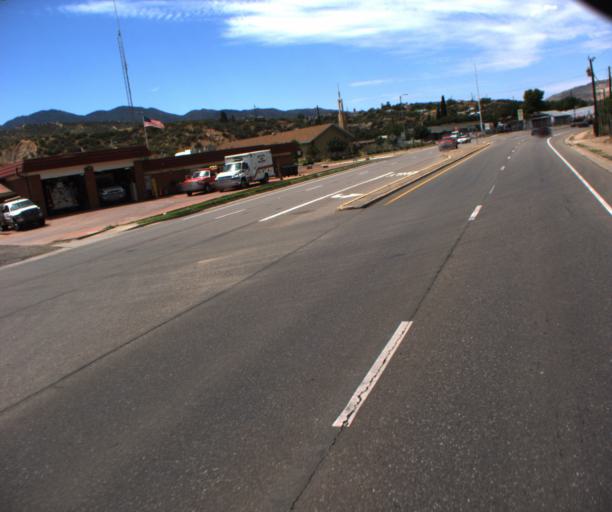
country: US
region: Arizona
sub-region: Gila County
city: Claypool
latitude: 33.4114
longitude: -110.8429
